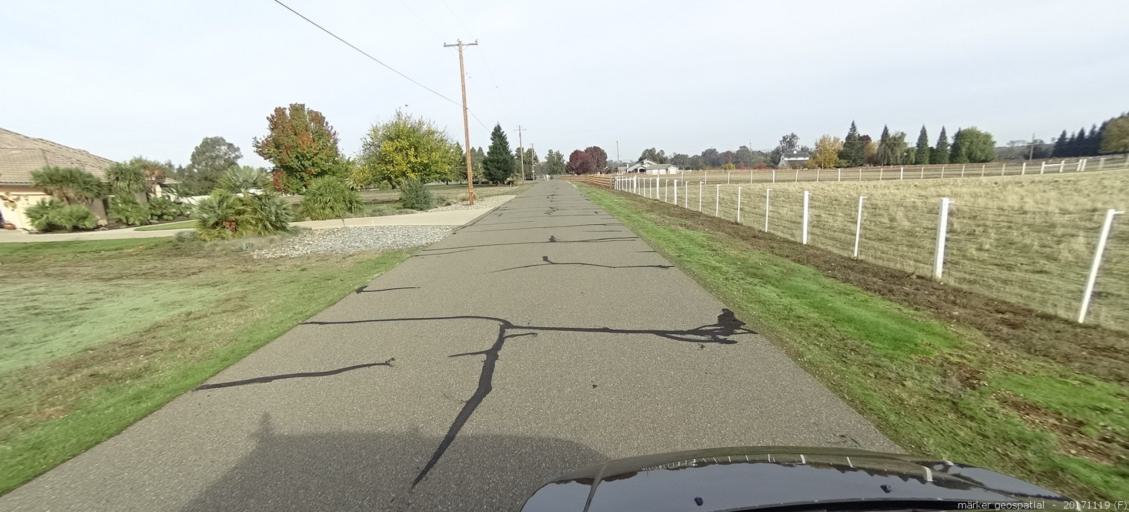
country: US
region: California
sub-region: Shasta County
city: Anderson
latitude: 40.5097
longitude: -122.3292
